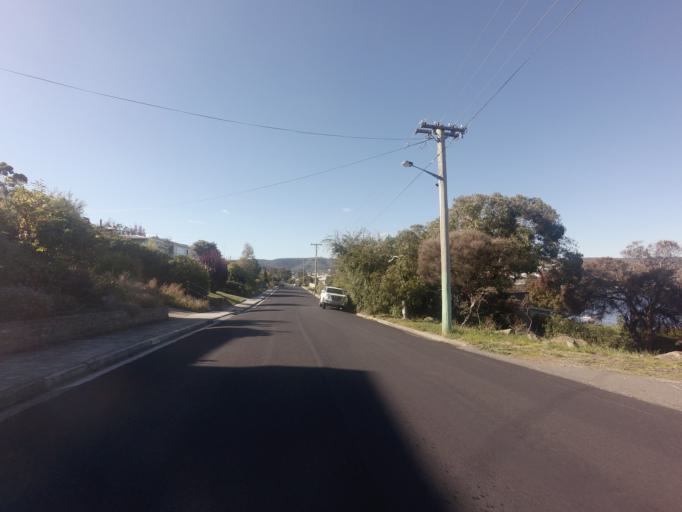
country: AU
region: Tasmania
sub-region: Clarence
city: Bellerive
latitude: -42.8722
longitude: 147.3607
